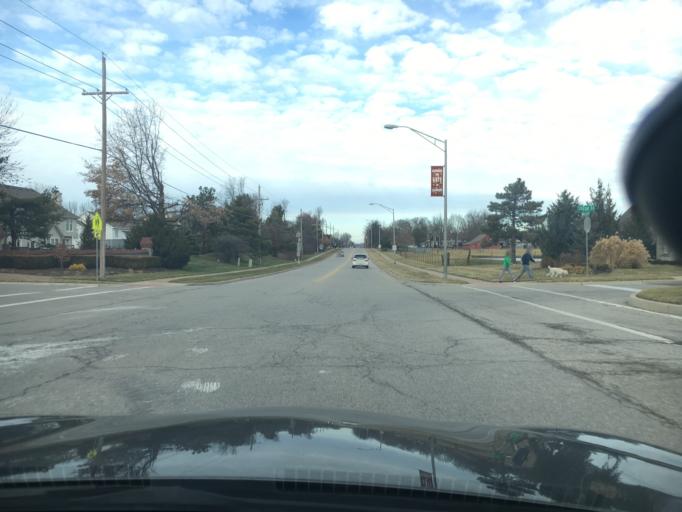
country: US
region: Kansas
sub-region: Johnson County
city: Leawood
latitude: 38.8885
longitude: -94.6305
